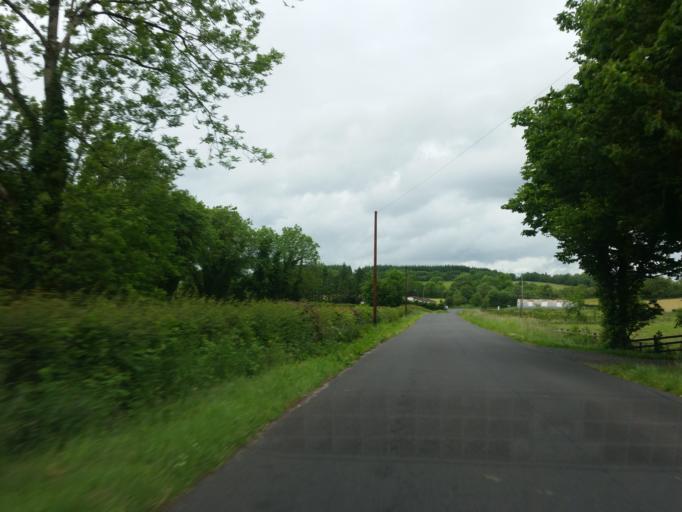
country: IE
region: Ulster
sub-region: County Monaghan
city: Clones
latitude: 54.2315
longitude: -7.2606
